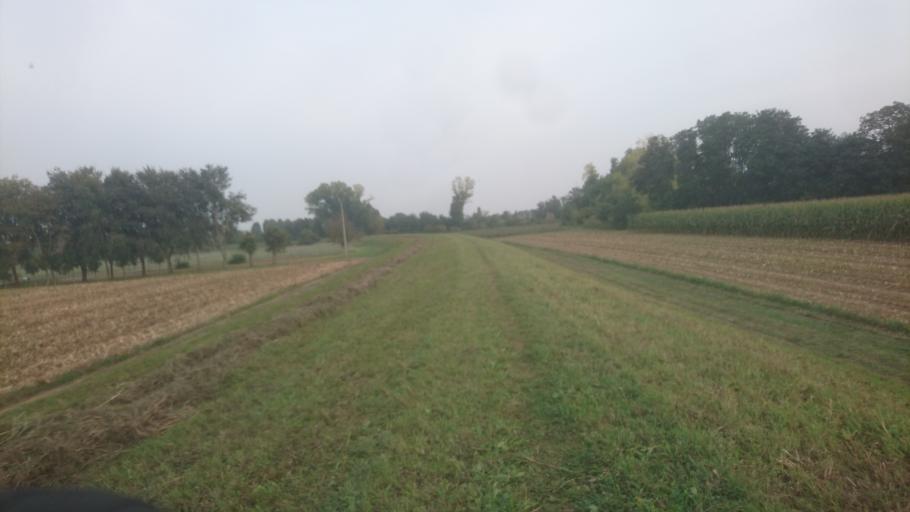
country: IT
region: Veneto
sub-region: Provincia di Padova
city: Veggiano
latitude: 45.4156
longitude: 11.7190
